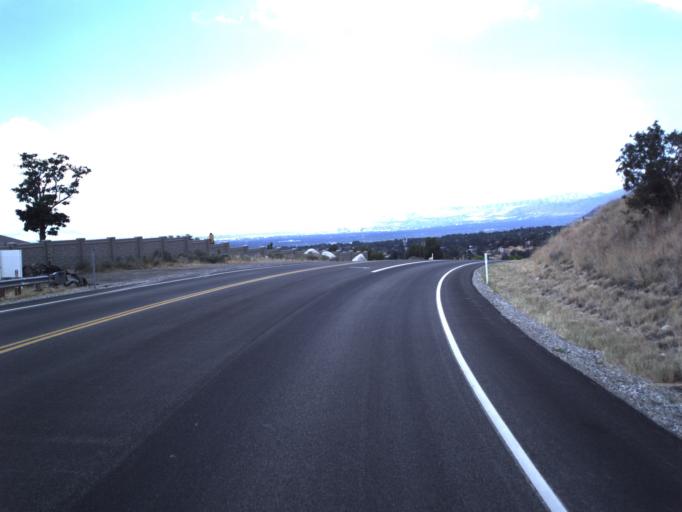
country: US
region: Utah
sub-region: Salt Lake County
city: Granite
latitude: 40.5805
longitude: -111.7921
